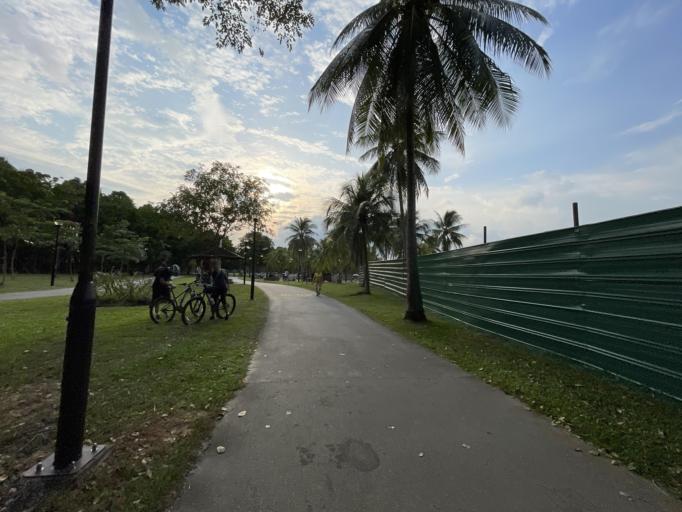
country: MY
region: Johor
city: Kampung Pasir Gudang Baru
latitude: 1.3810
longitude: 103.9591
